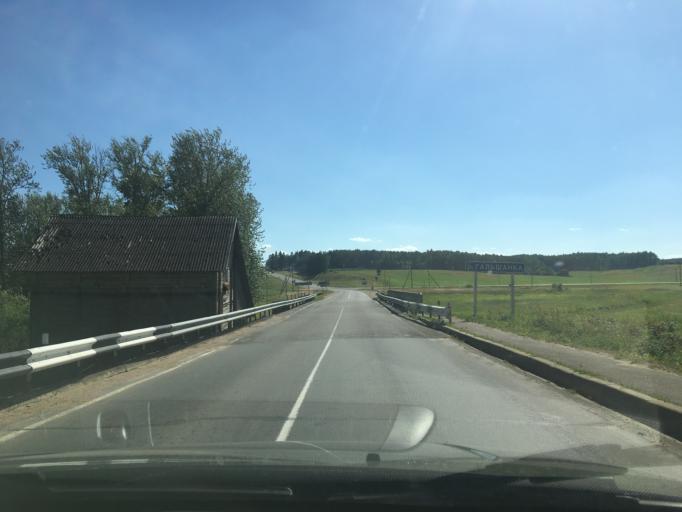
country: BY
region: Grodnenskaya
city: Hal'shany
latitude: 54.2555
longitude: 26.0093
